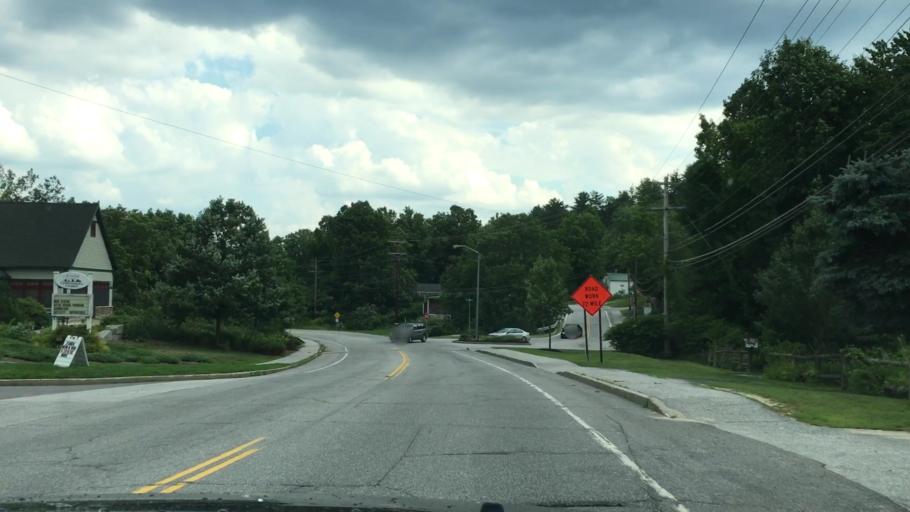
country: US
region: New Hampshire
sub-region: Belknap County
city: Meredith
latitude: 43.6669
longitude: -71.5027
